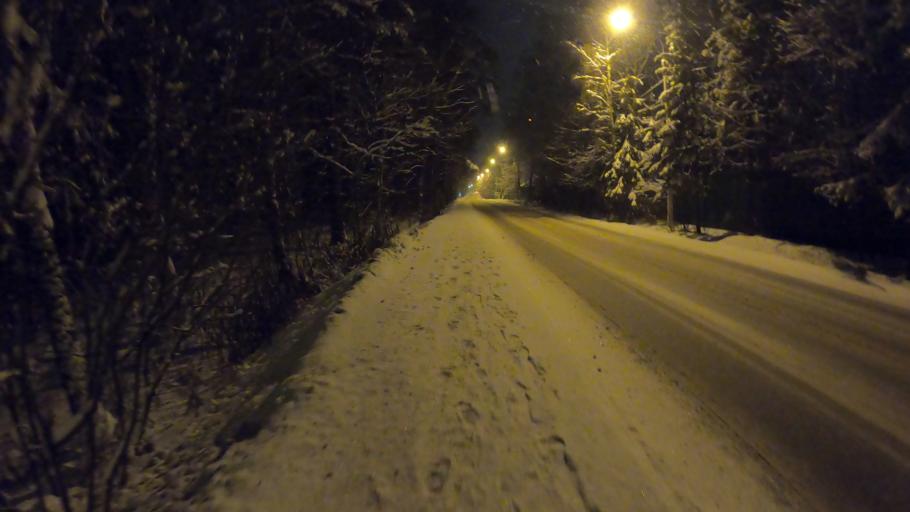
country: RU
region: Moskovskaya
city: Opalikha
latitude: 55.8360
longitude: 37.2193
